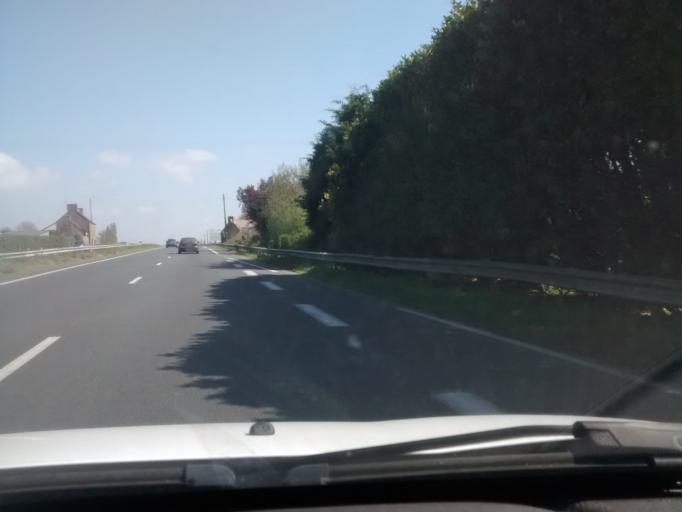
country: FR
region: Brittany
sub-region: Departement des Cotes-d'Armor
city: Saint-Agathon
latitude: 48.5499
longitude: -3.1095
